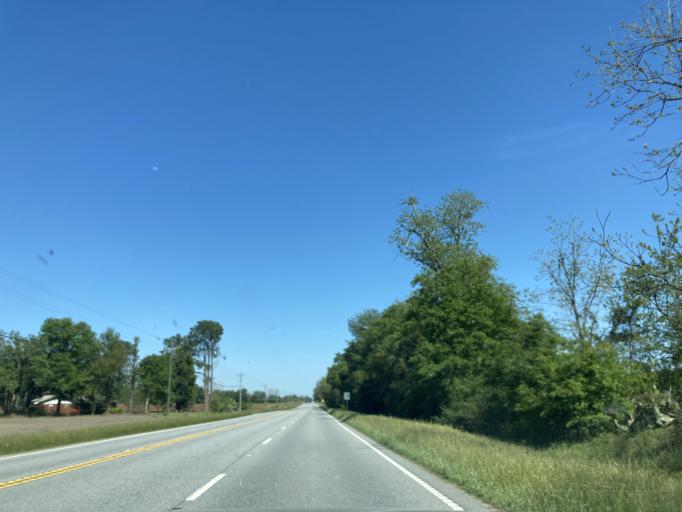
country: US
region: Georgia
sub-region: Miller County
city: Colquitt
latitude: 31.1852
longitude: -84.5997
